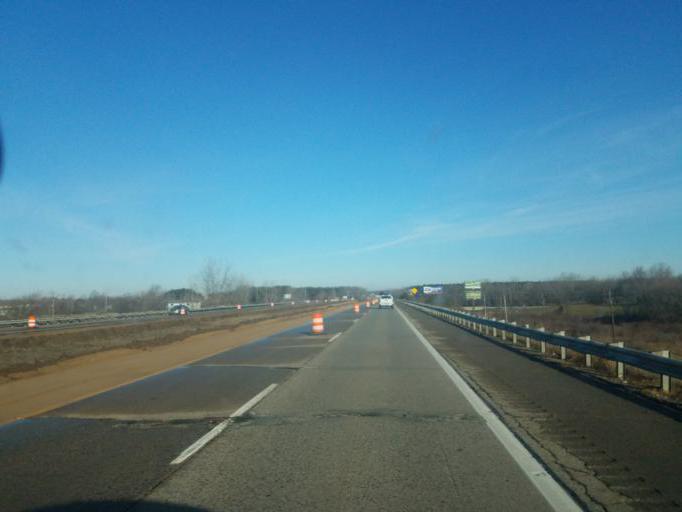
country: US
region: Michigan
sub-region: Gratiot County
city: Saint Louis
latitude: 43.3931
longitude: -84.6260
